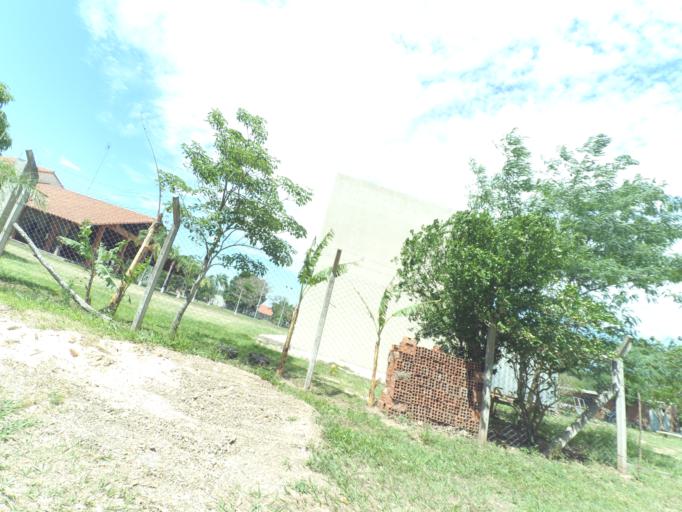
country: BO
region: Santa Cruz
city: Santa Cruz de la Sierra
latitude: -17.8118
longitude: -63.2354
